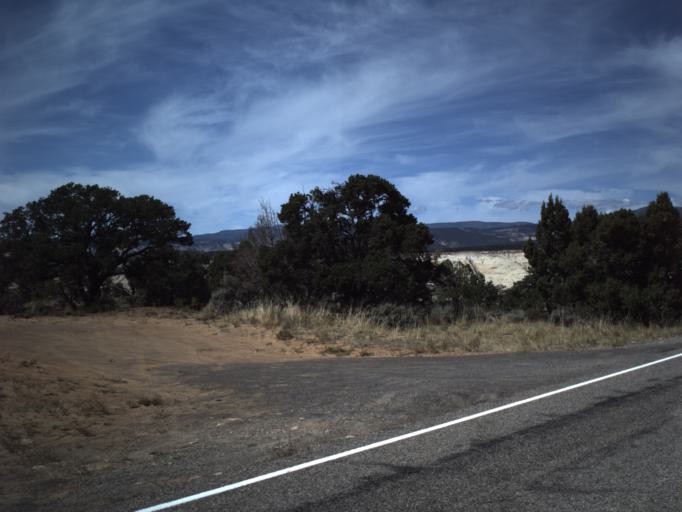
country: US
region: Utah
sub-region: Wayne County
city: Loa
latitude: 37.8559
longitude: -111.4338
